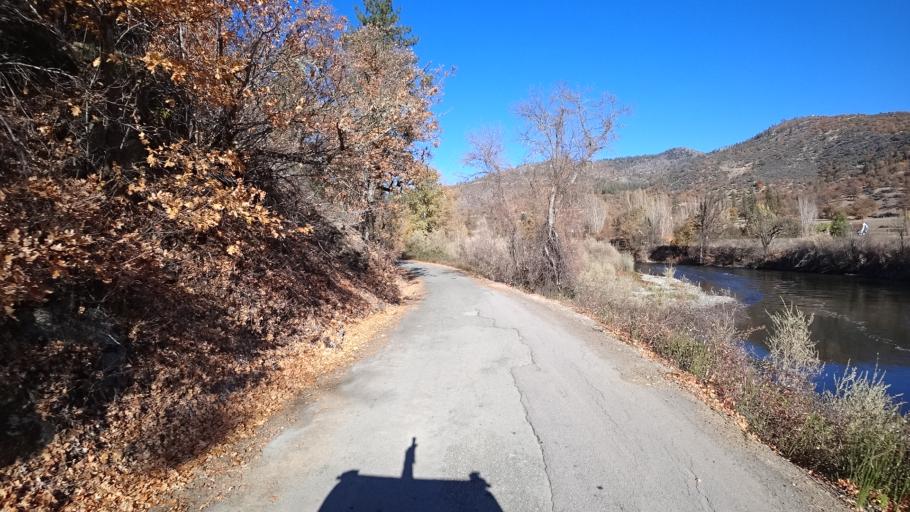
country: US
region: California
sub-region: Siskiyou County
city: Yreka
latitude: 41.8387
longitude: -122.8721
